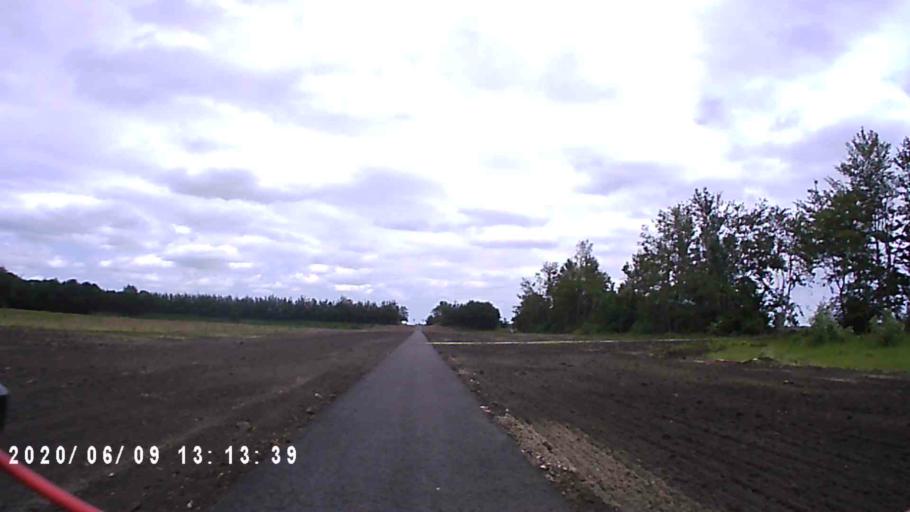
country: NL
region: Groningen
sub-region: Gemeente Haren
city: Haren
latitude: 53.2131
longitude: 6.6672
